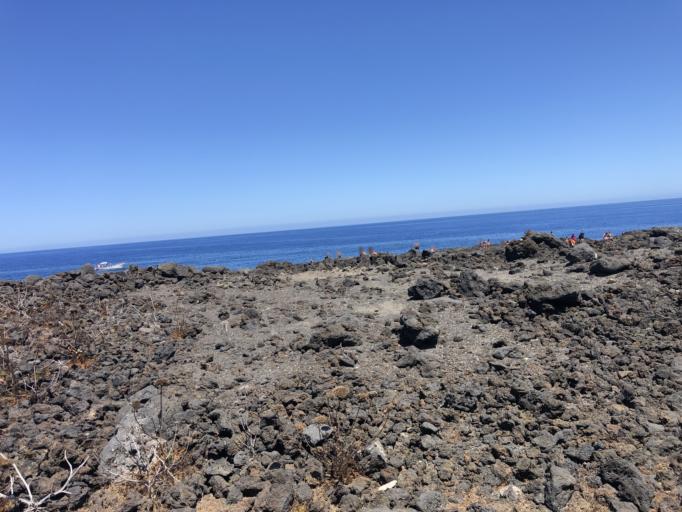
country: IT
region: Sicily
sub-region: Agrigento
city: Lampedusa
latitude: 35.8743
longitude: 12.8776
